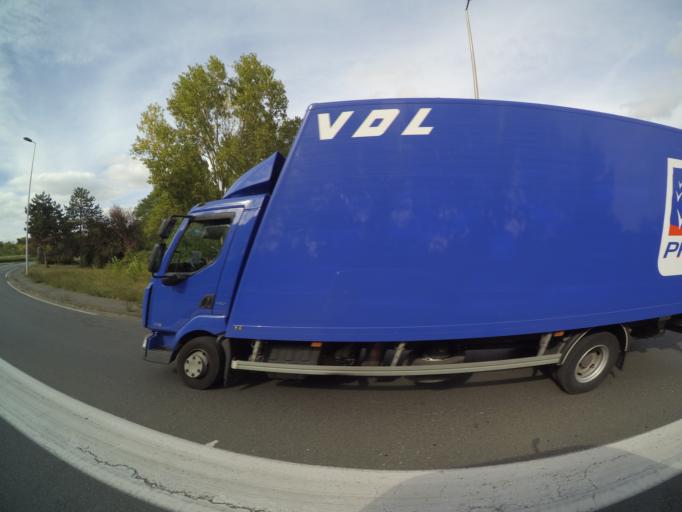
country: FR
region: Centre
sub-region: Departement d'Indre-et-Loire
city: Saint-Pierre-des-Corps
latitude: 47.4036
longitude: 0.7255
